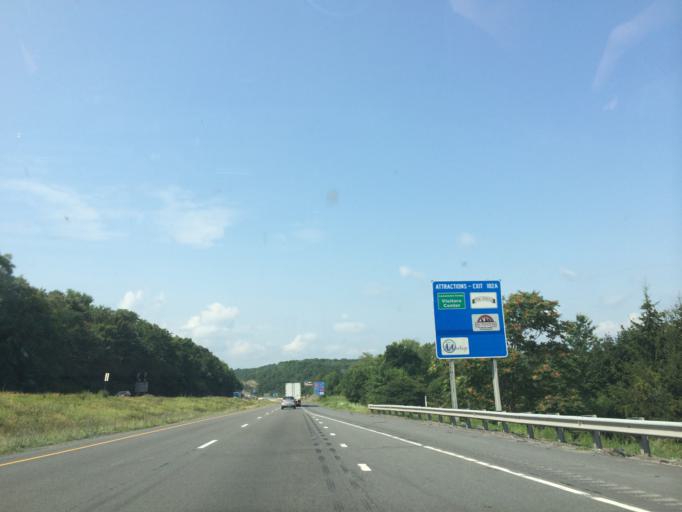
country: US
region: Pennsylvania
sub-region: Lackawanna County
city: Scranton
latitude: 41.3897
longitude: -75.6565
